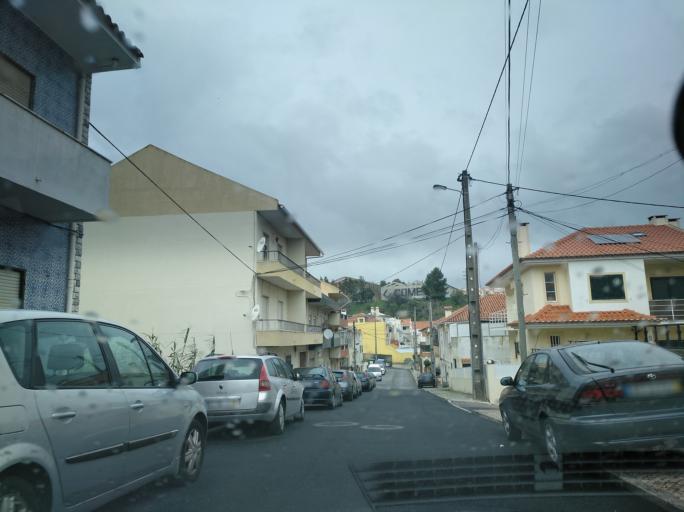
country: PT
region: Lisbon
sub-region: Odivelas
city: Famoes
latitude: 38.7892
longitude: -9.2038
